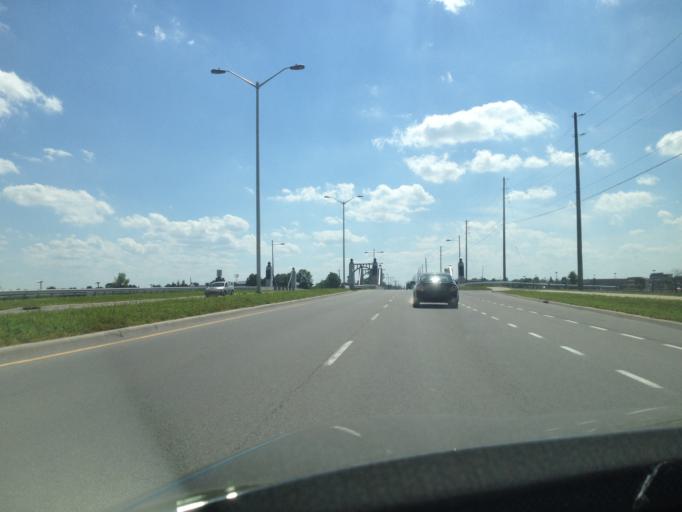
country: CA
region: Ontario
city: Bells Corners
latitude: 45.2916
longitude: -75.8989
